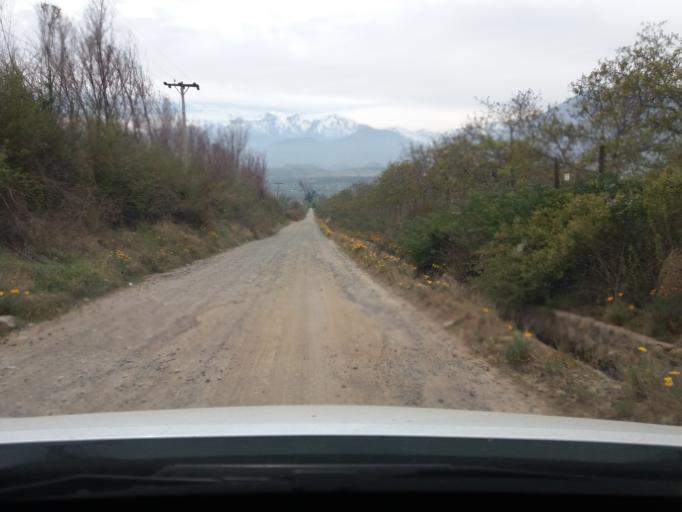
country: CL
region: Valparaiso
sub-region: Provincia de Los Andes
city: Los Andes
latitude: -32.8437
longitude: -70.5525
